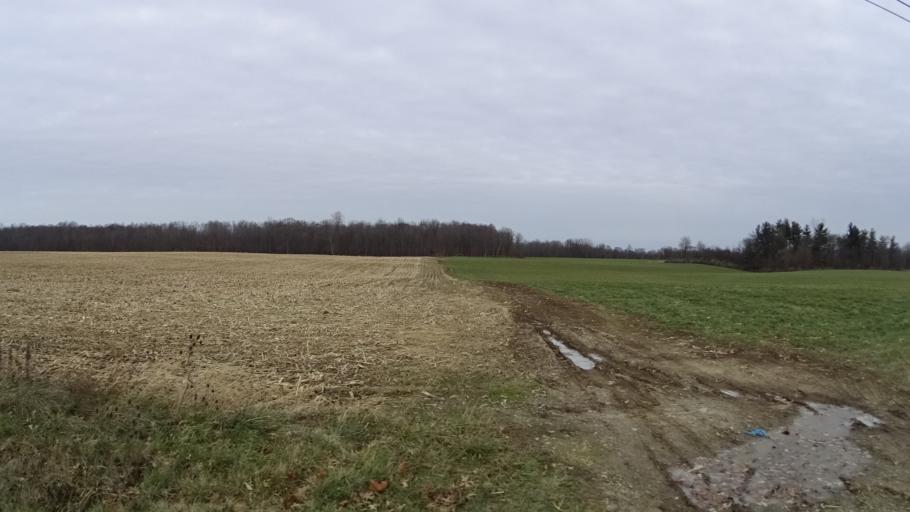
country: US
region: Ohio
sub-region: Lorain County
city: Wellington
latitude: 41.1902
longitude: -82.2539
